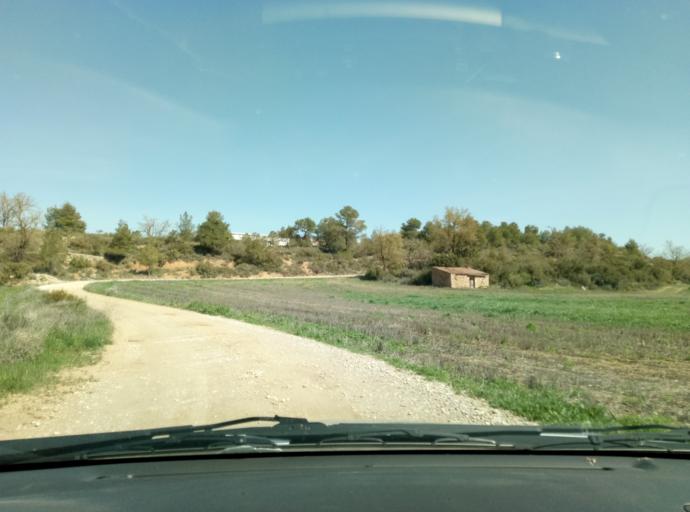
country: ES
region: Catalonia
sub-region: Provincia de Lleida
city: Vinaixa
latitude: 41.4165
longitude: 0.9185
